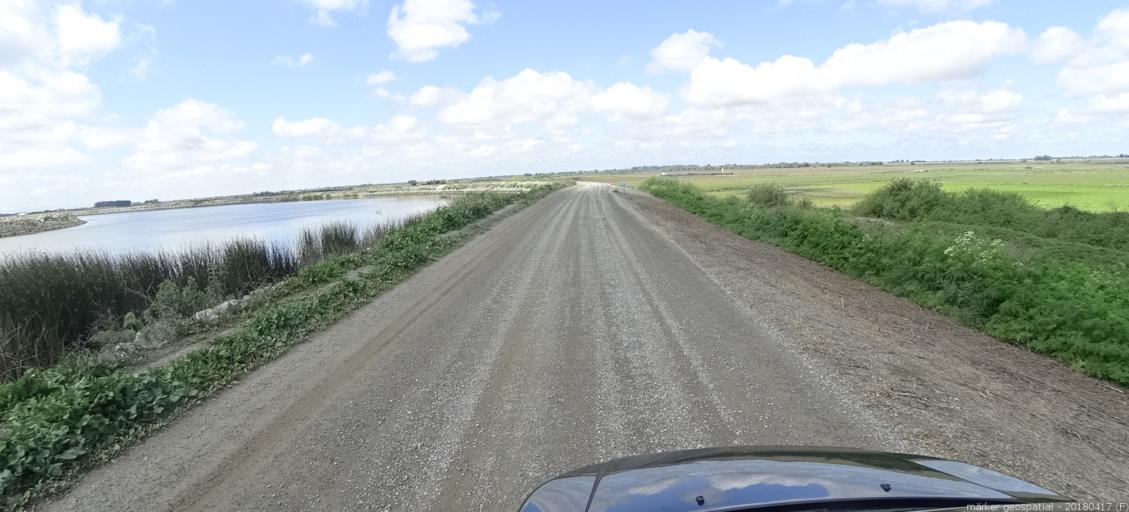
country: US
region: California
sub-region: Sacramento County
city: Walnut Grove
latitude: 38.1522
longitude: -121.5391
